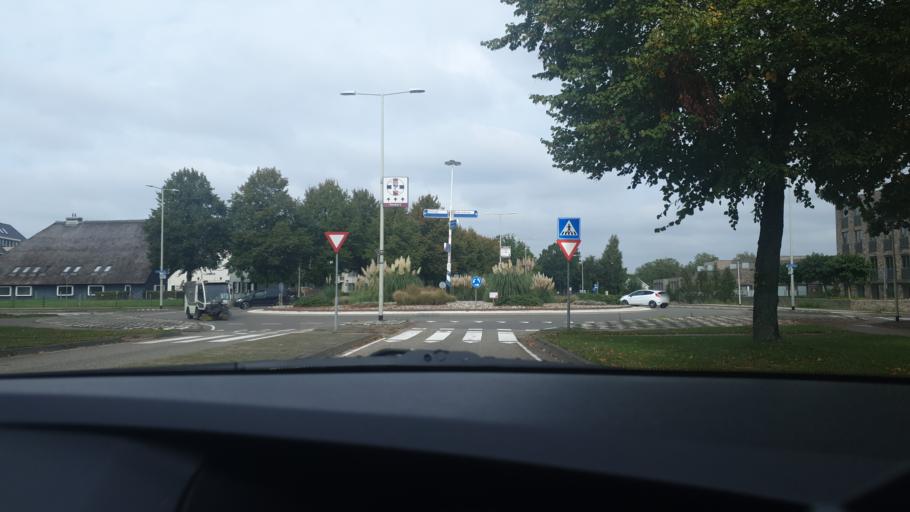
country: NL
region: North Brabant
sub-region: Gemeente Bergen op Zoom
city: Halsteren
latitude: 51.5205
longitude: 4.2752
